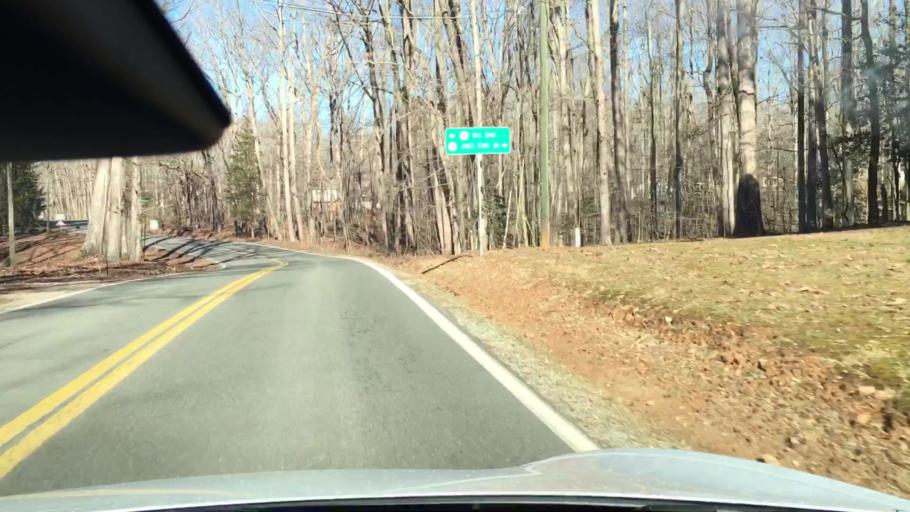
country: US
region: Virginia
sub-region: Powhatan County
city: Powhatan
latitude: 37.5599
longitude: -77.7996
